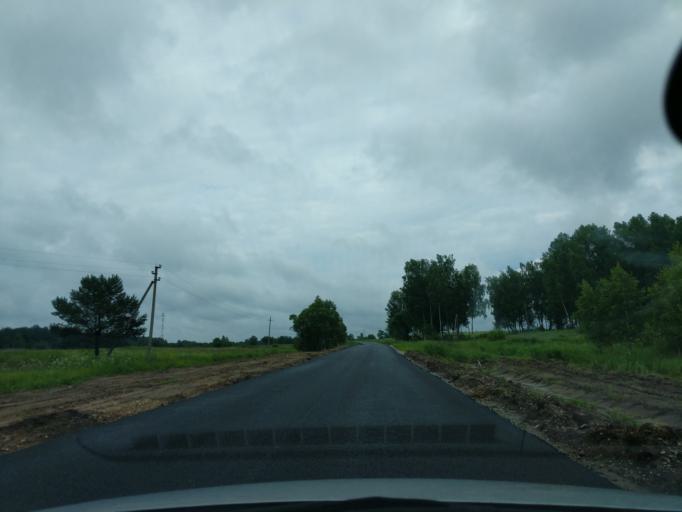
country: RU
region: Kaluga
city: Myatlevo
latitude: 54.8025
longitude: 35.7102
